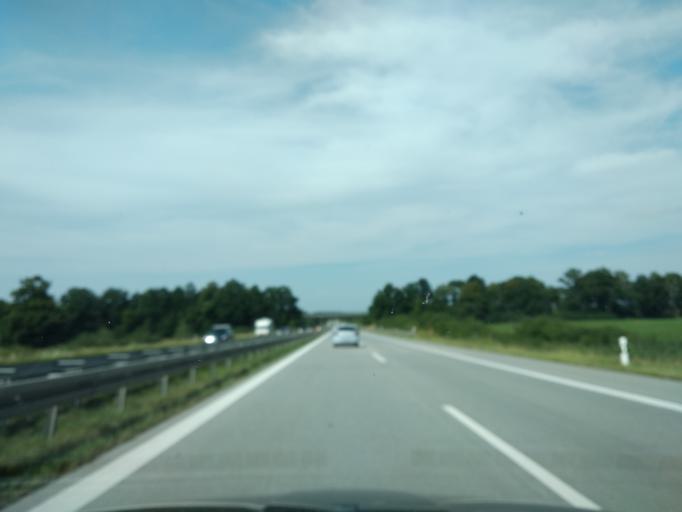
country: DE
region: Brandenburg
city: Althuttendorf
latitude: 52.9686
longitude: 13.8153
